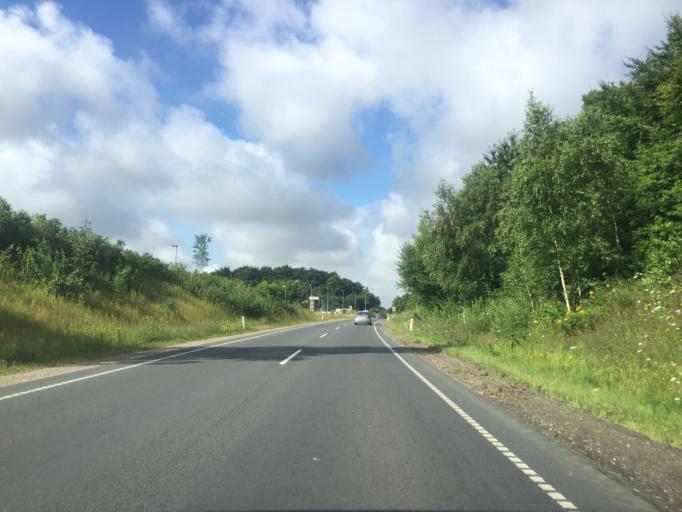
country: DK
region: South Denmark
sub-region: Svendborg Kommune
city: Svendborg
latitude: 55.0758
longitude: 10.5989
